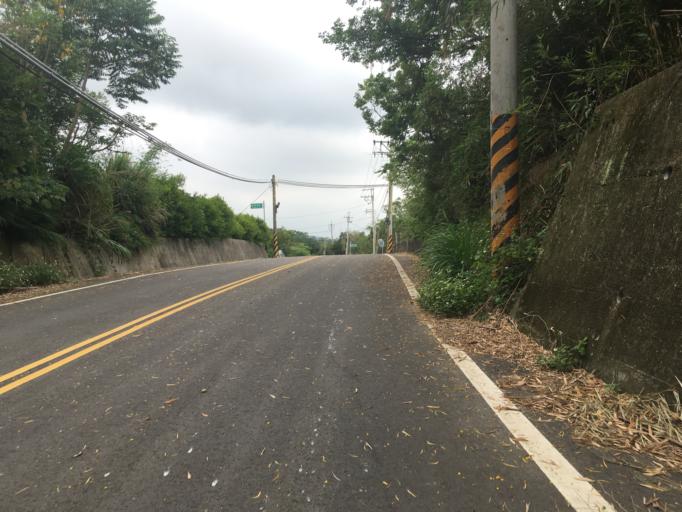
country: TW
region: Taiwan
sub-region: Hsinchu
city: Hsinchu
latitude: 24.7418
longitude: 120.9824
